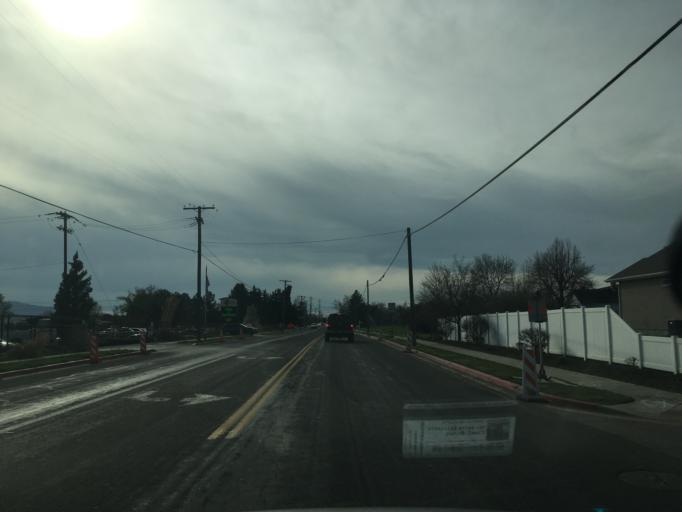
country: US
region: Utah
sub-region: Davis County
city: Layton
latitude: 41.0602
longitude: -111.9993
